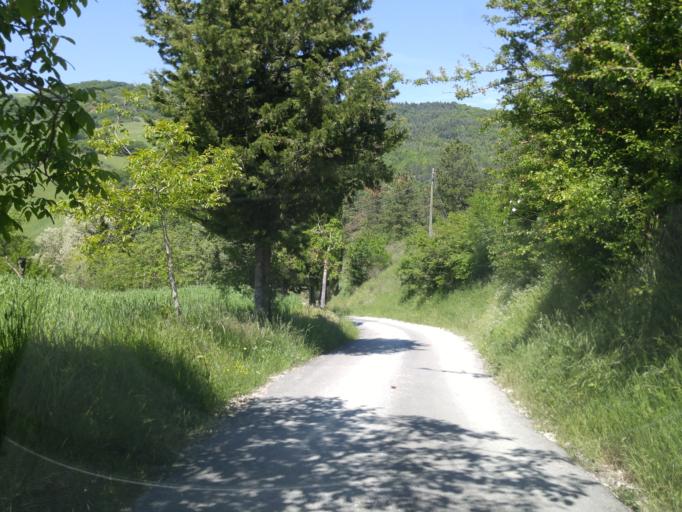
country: IT
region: The Marches
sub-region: Provincia di Pesaro e Urbino
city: Canavaccio
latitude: 43.7169
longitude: 12.6851
